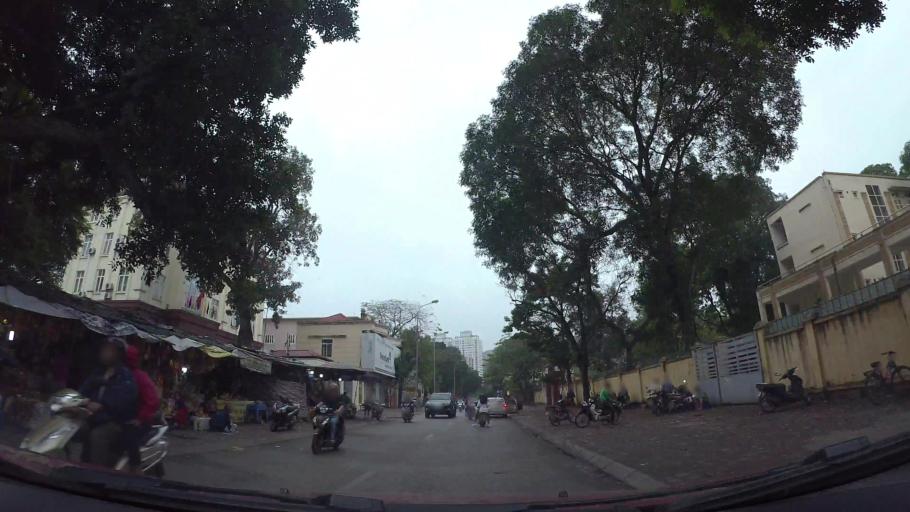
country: VN
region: Ha Noi
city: Hai BaTrung
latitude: 21.0060
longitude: 105.8352
